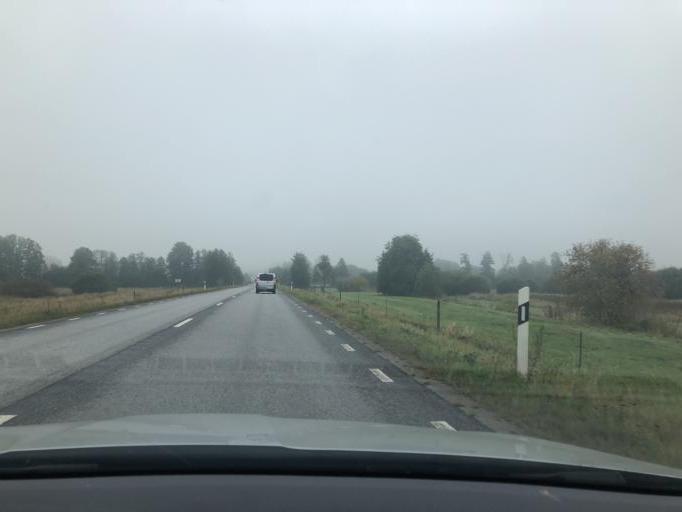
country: SE
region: Uppsala
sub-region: Tierps Kommun
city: Tierp
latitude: 60.3288
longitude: 17.5138
